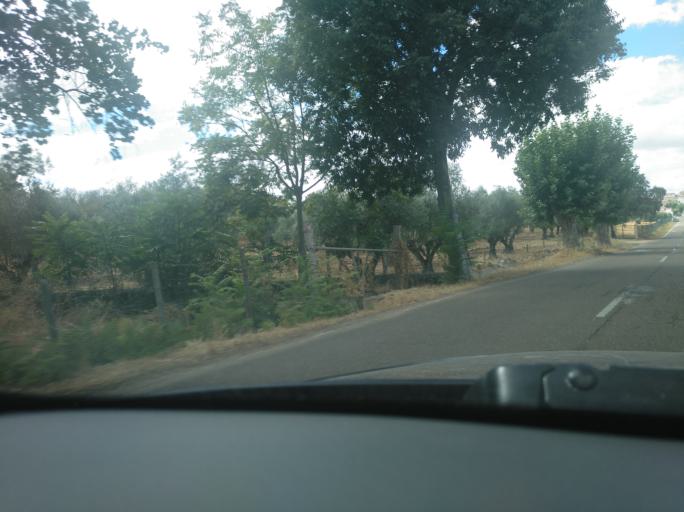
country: PT
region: Portalegre
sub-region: Arronches
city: Arronches
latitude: 39.0485
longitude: -7.4337
